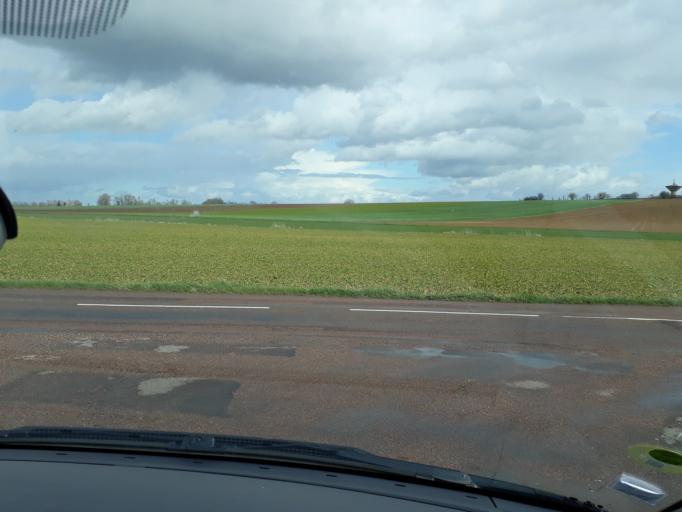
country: FR
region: Bourgogne
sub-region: Departement de la Cote-d'Or
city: Genlis
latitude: 47.2170
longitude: 5.1928
